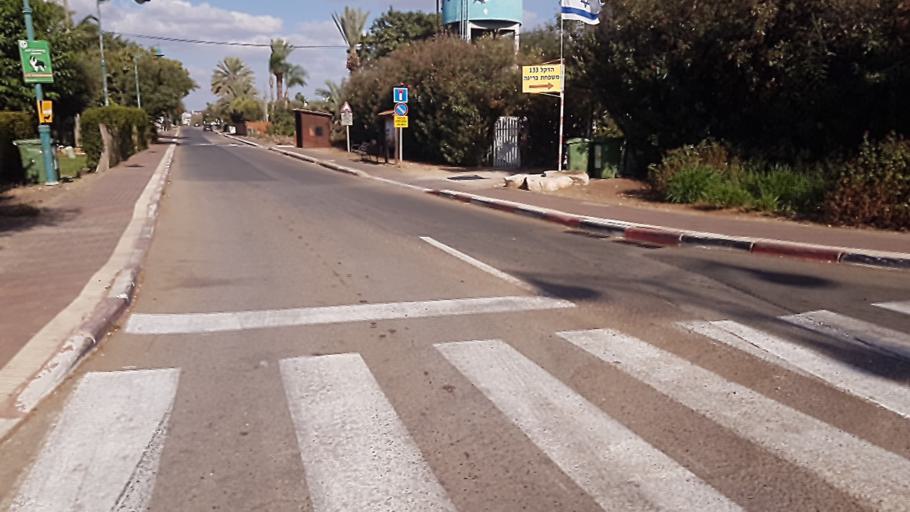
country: IL
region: Central District
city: Jaljulya
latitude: 32.1744
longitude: 34.9391
